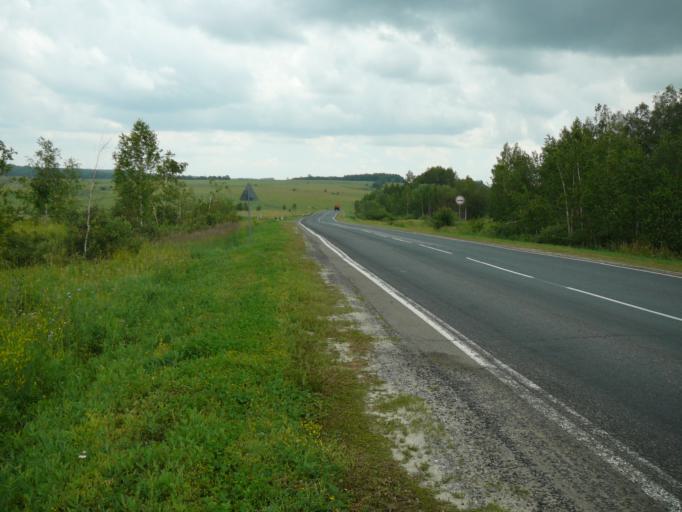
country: RU
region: Nizjnij Novgorod
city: Lukoyanov
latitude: 54.9264
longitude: 44.6664
